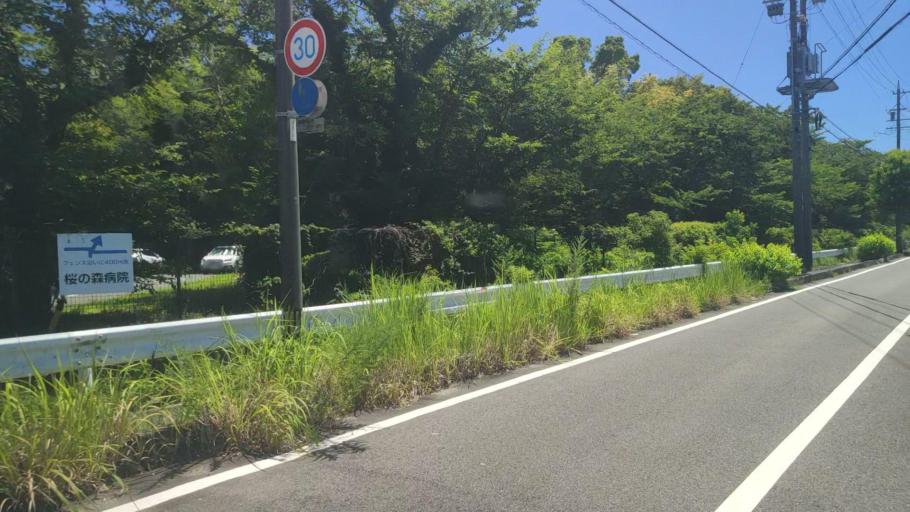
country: JP
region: Mie
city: Suzuka
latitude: 34.8529
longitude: 136.5865
